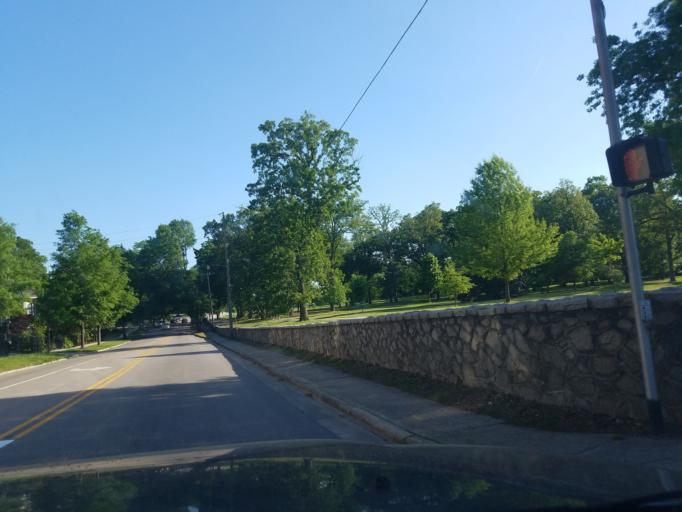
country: US
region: North Carolina
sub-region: Durham County
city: Durham
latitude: 36.0055
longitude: -78.9124
